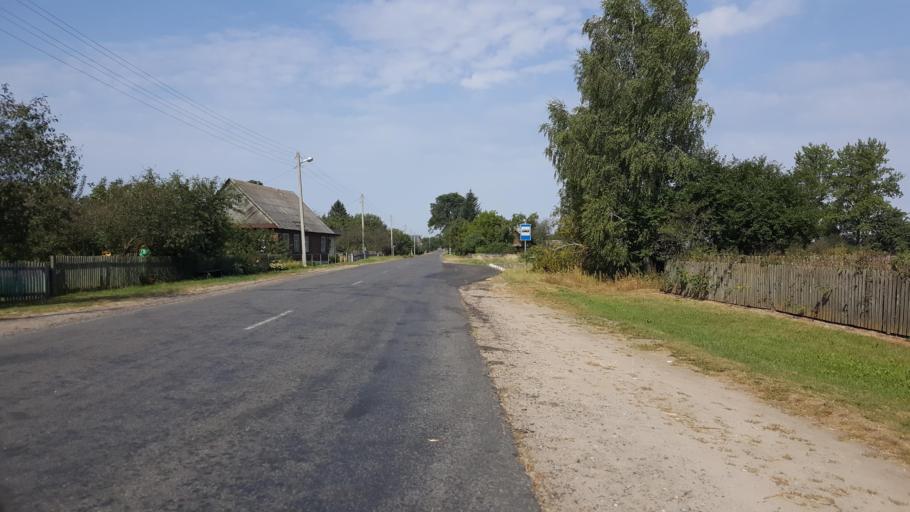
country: BY
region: Brest
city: Kamyanyets
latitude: 52.4260
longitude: 23.7669
